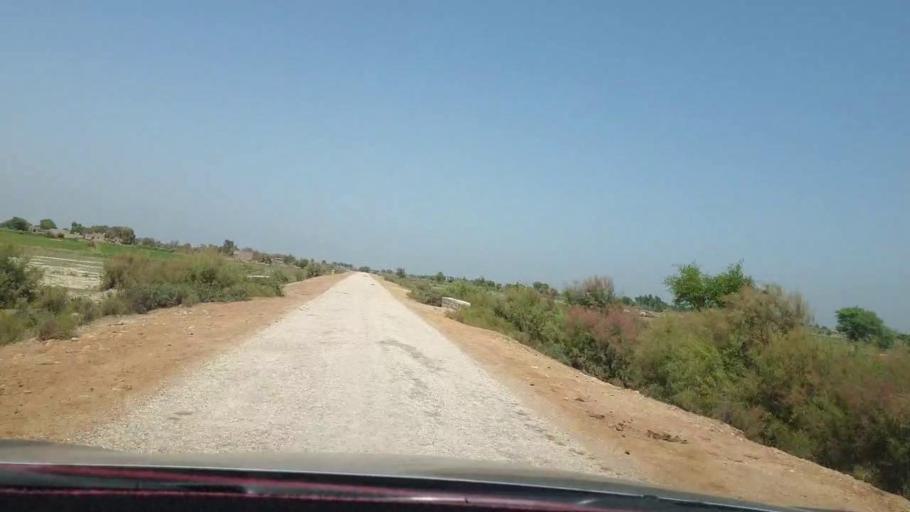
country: PK
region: Sindh
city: Warah
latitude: 27.5149
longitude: 67.7066
